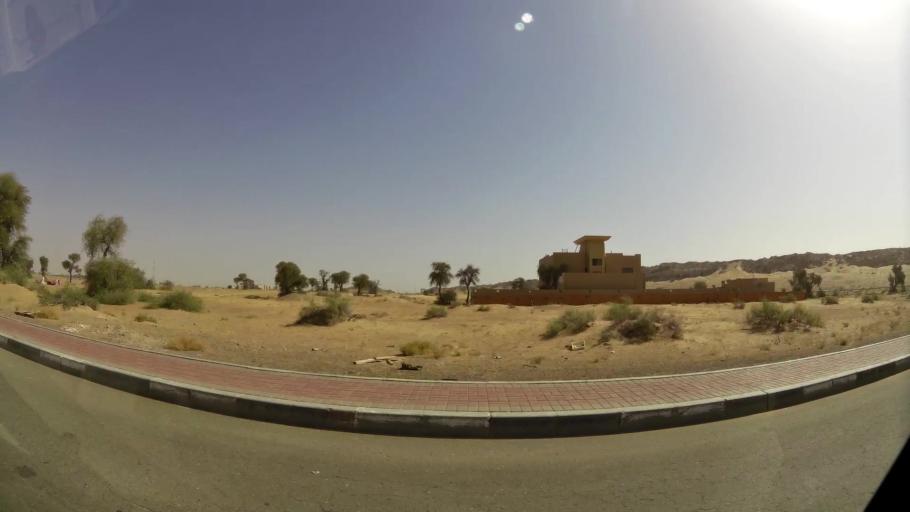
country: OM
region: Al Buraimi
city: Al Buraymi
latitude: 24.3218
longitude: 55.8101
